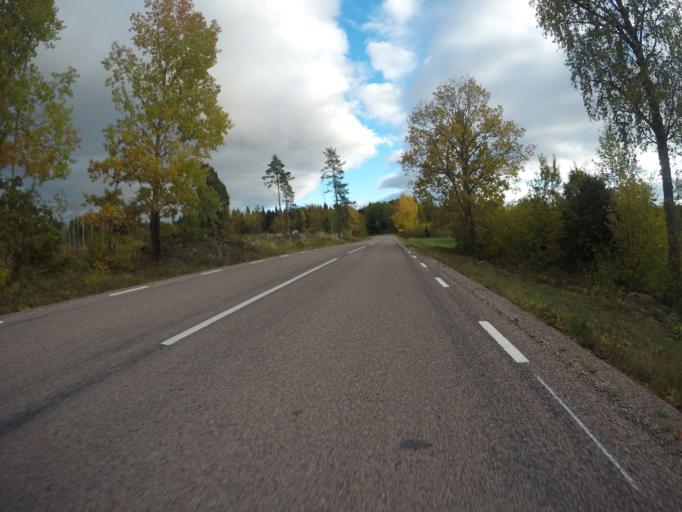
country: SE
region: Vaestmanland
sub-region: Arboga Kommun
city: Tyringe
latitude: 59.3130
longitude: 15.9857
